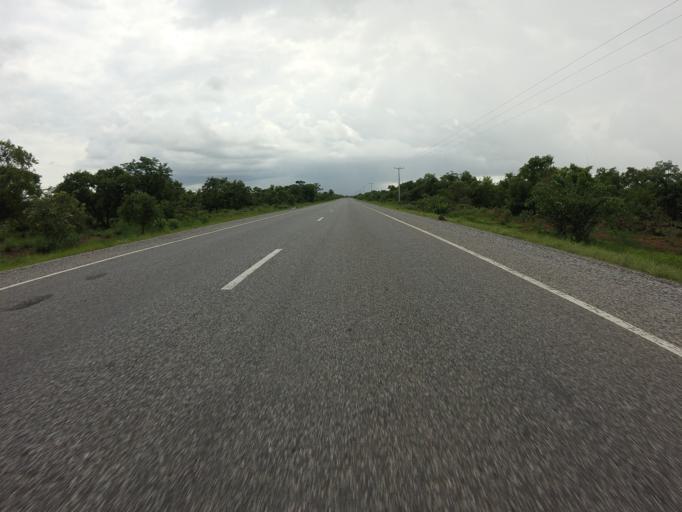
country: GH
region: Northern
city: Tamale
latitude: 9.1331
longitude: -1.3221
